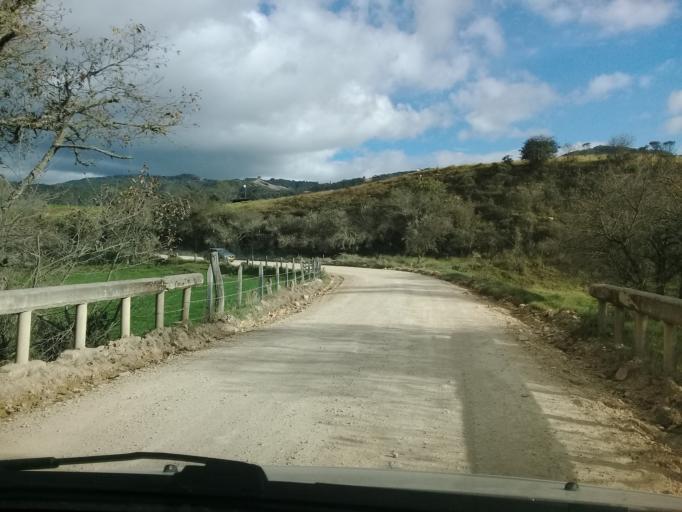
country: CO
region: Cundinamarca
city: Lenguazaque
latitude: 5.2771
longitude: -73.6555
